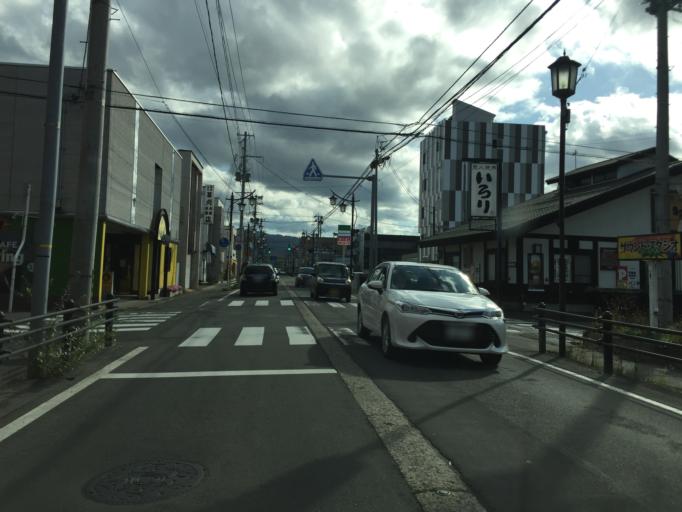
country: JP
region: Yamagata
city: Yonezawa
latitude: 37.9138
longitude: 140.1095
